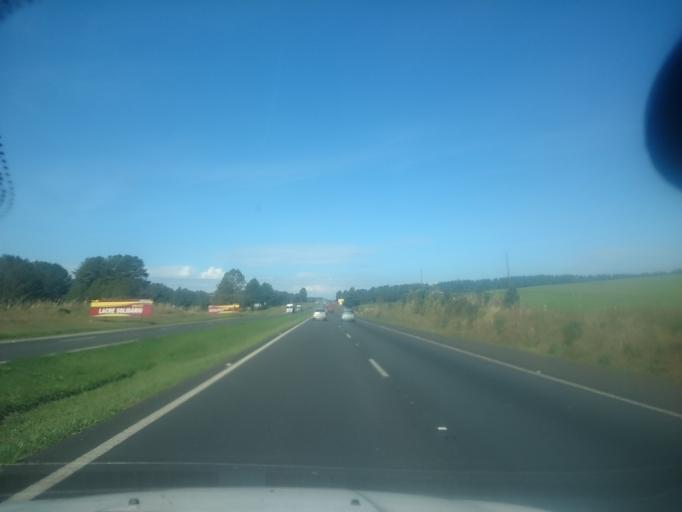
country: BR
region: Parana
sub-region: Campo Largo
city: Campo Largo
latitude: -25.4518
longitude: -49.7378
